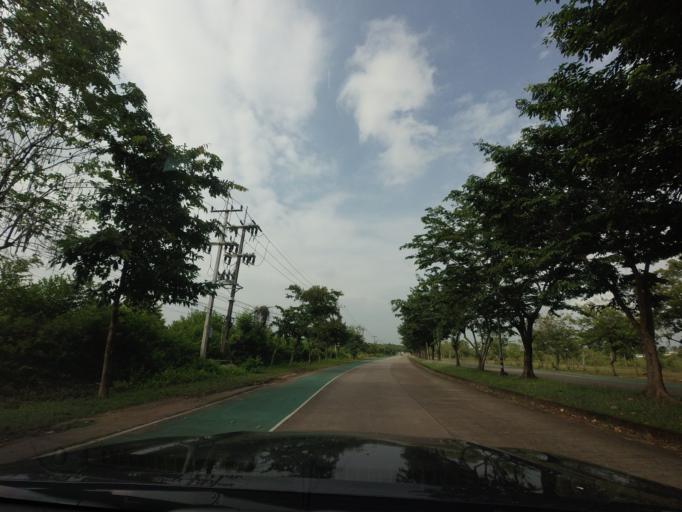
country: TH
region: Nong Khai
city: Nong Khai
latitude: 17.8136
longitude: 102.7491
